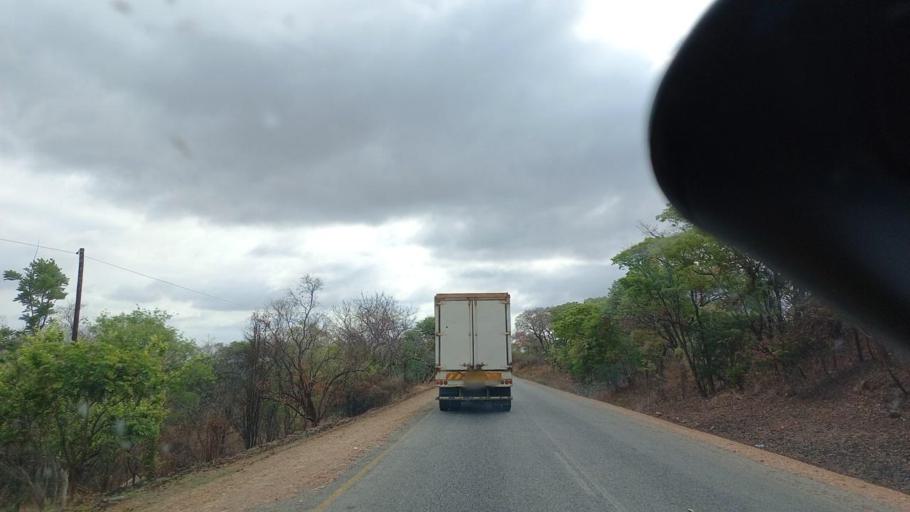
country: ZM
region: Lusaka
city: Chongwe
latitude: -15.1309
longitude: 29.5241
